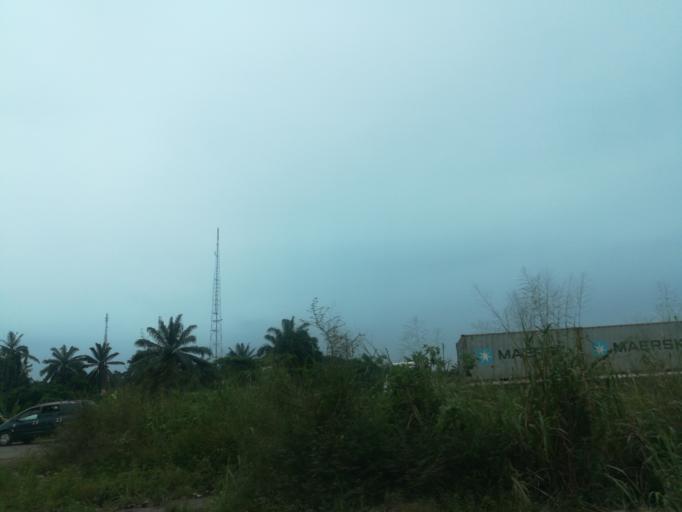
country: NG
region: Oyo
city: Ibadan
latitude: 7.3898
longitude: 3.9363
